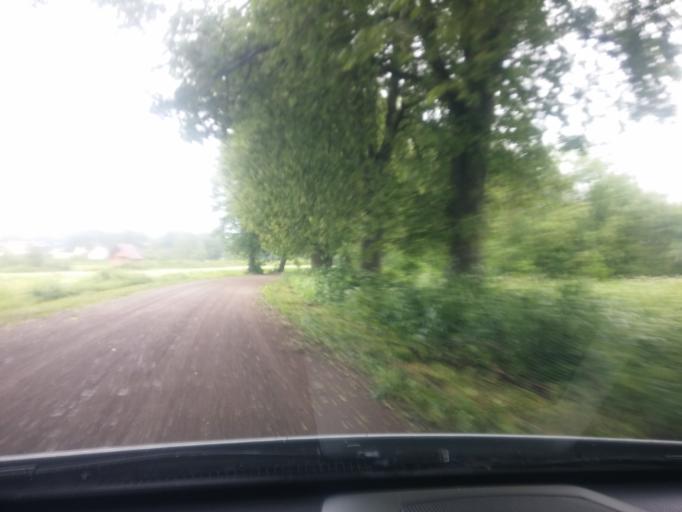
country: LV
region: Ogre
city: Ogre
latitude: 56.8636
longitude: 24.5776
